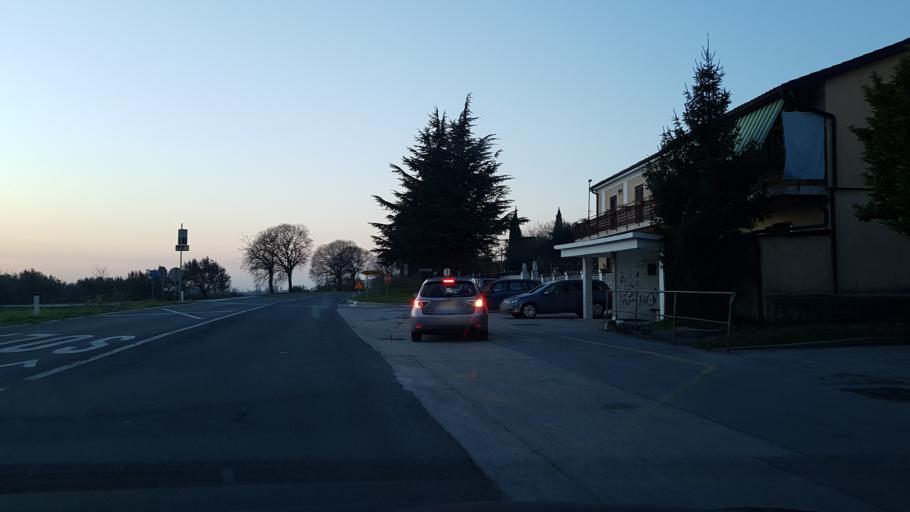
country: SI
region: Koper-Capodistria
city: Dekani
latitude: 45.5466
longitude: 13.8075
